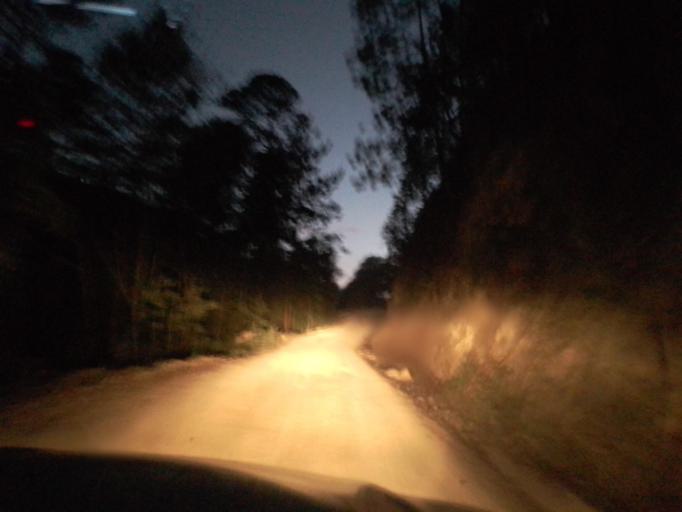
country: GT
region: San Marcos
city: Tacana
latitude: 15.2374
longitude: -92.1973
